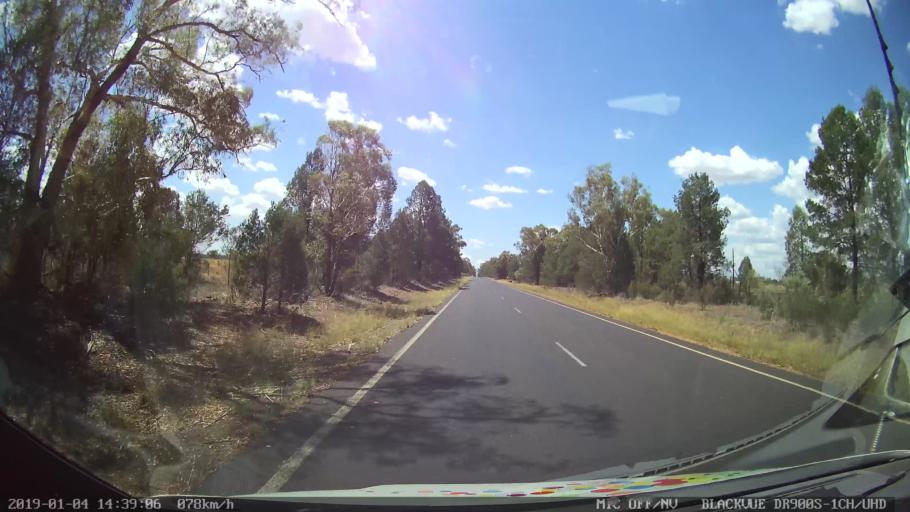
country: AU
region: New South Wales
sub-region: Dubbo Municipality
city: Dubbo
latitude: -32.1688
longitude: 148.6323
